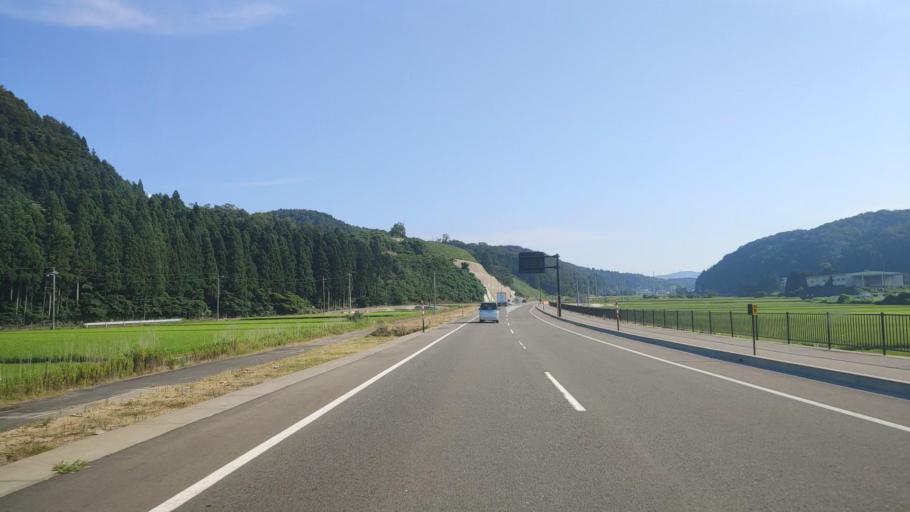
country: JP
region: Fukui
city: Maruoka
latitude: 36.2045
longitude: 136.2678
